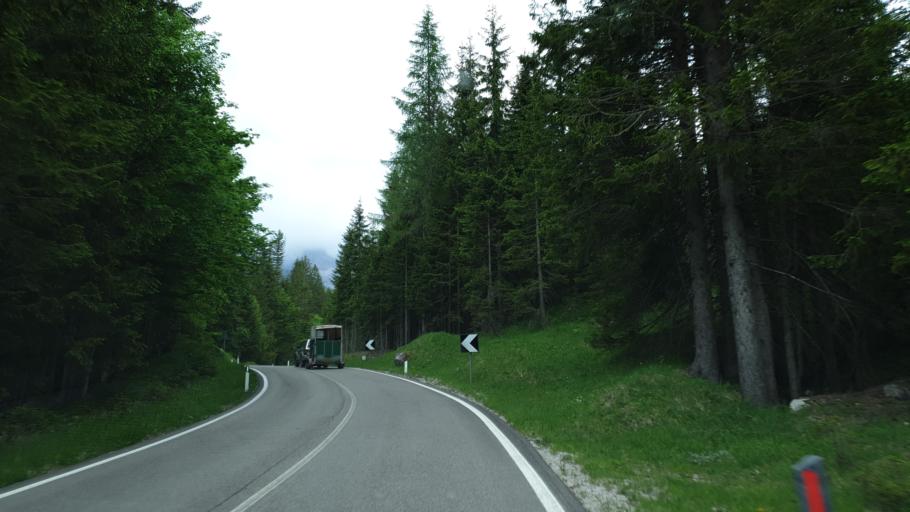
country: IT
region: Veneto
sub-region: Provincia di Belluno
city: San Vito
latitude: 46.5400
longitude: 12.2550
